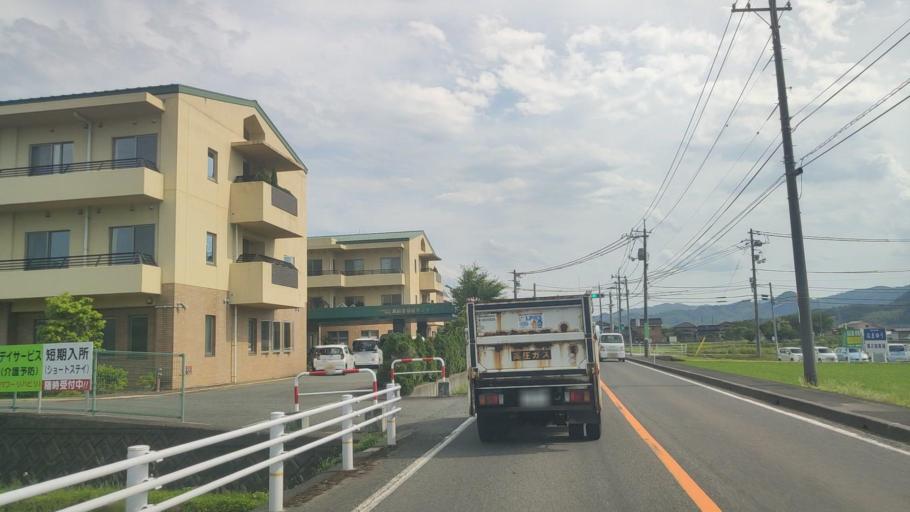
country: JP
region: Tottori
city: Tottori
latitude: 35.4754
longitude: 134.2050
